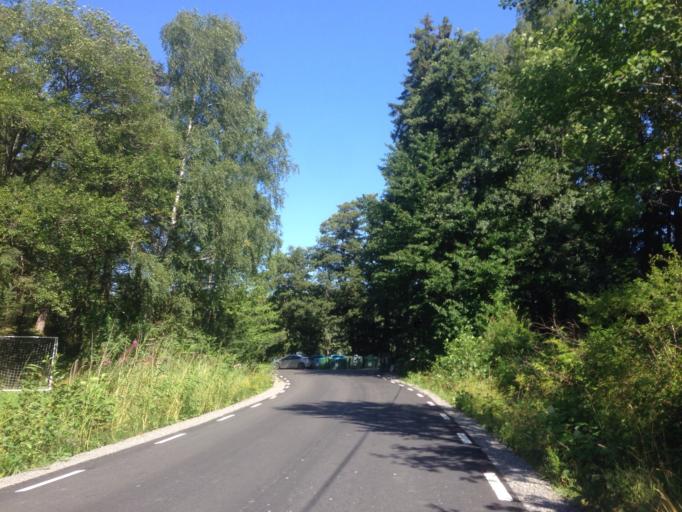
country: SE
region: Stockholm
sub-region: Vaxholms Kommun
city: Vaxholm
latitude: 59.3861
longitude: 18.3684
